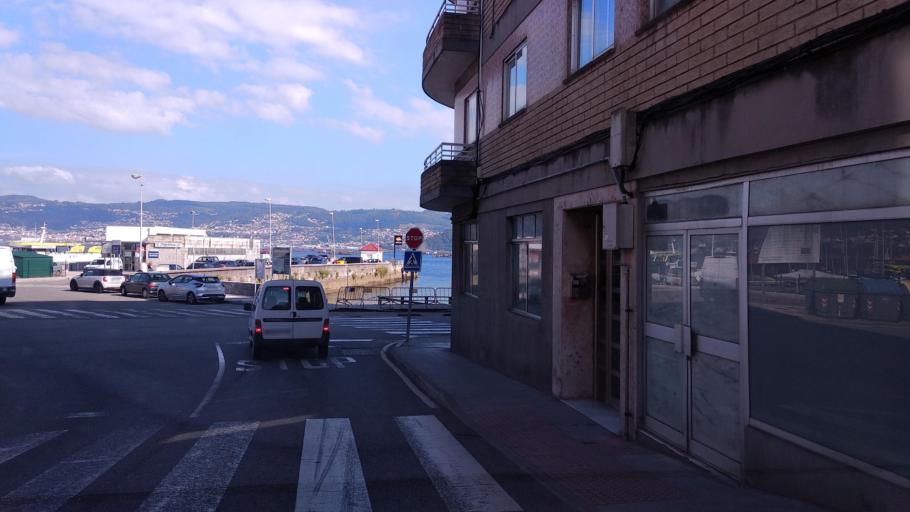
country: ES
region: Galicia
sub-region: Provincia de Pontevedra
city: Moana
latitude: 42.2755
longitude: -8.7367
